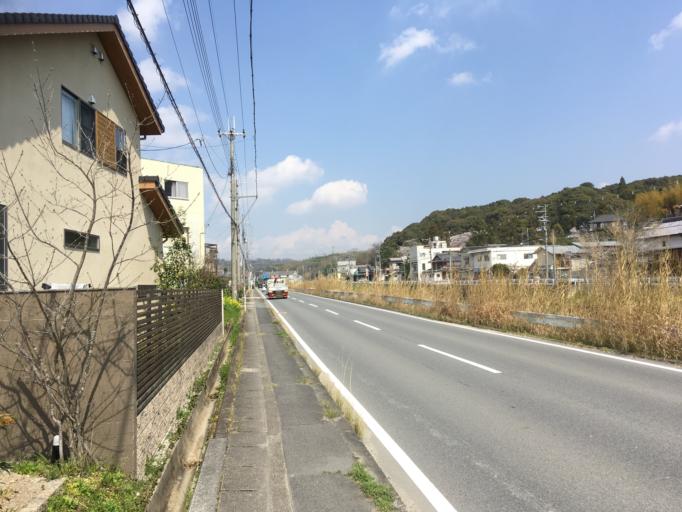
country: JP
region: Nara
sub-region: Ikoma-shi
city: Ikoma
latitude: 34.7424
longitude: 135.7214
